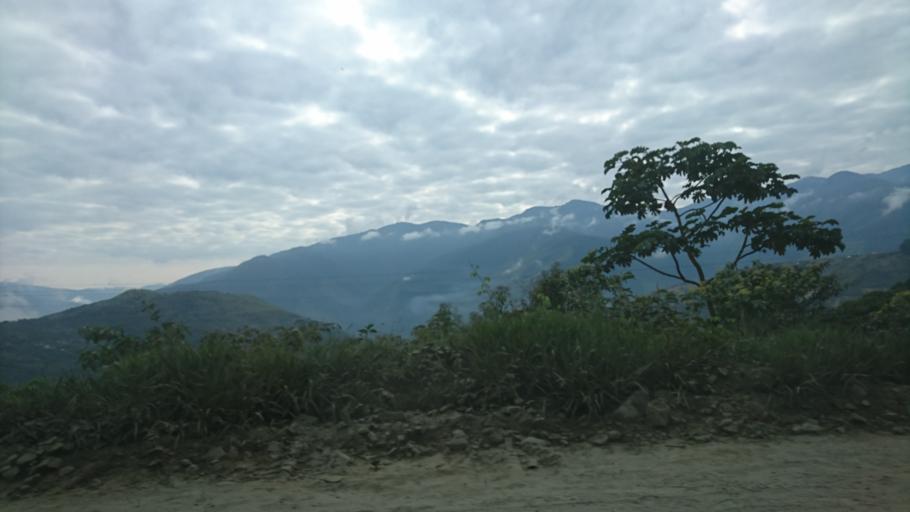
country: BO
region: La Paz
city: Coroico
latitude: -16.1980
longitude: -67.7064
